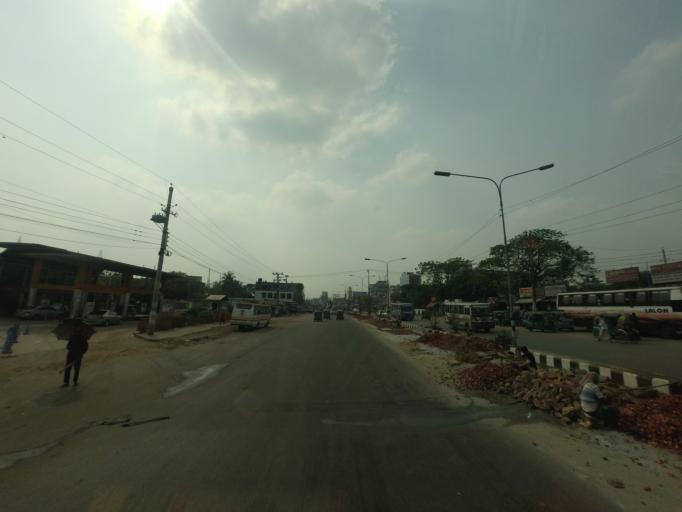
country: BD
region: Dhaka
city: Azimpur
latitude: 23.7825
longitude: 90.3493
